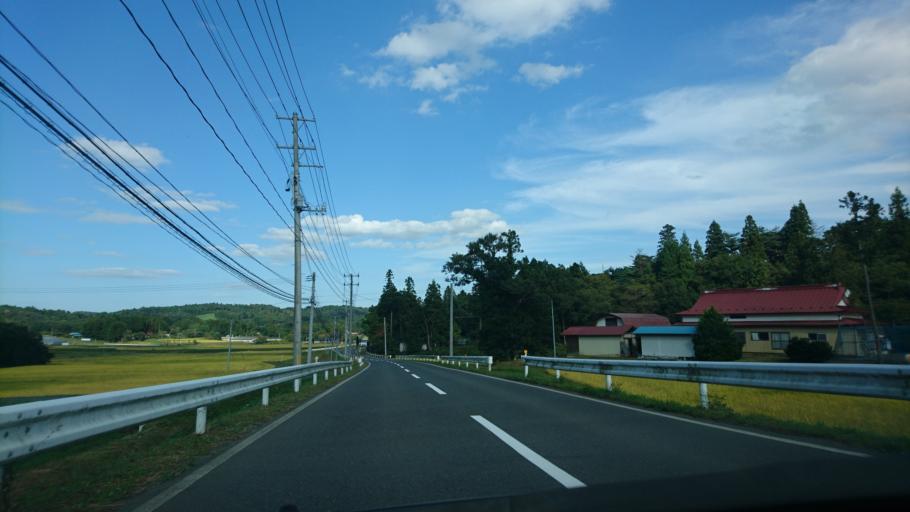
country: JP
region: Iwate
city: Ichinoseki
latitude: 38.8332
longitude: 141.2276
